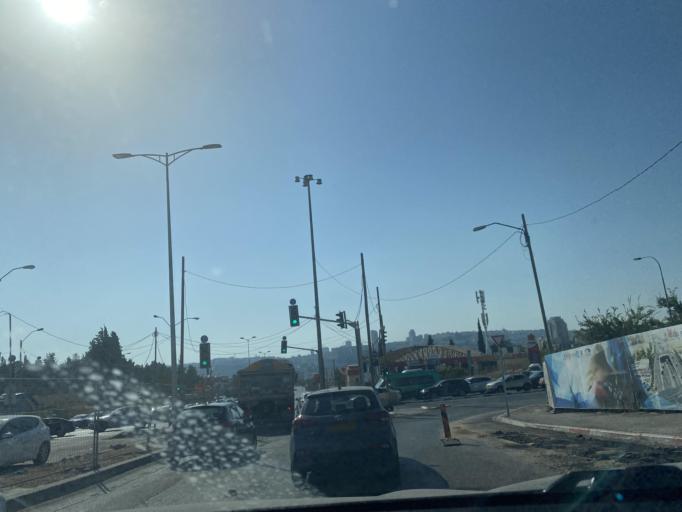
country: IL
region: Jerusalem
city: Jerusalem
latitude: 31.7455
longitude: 35.2140
